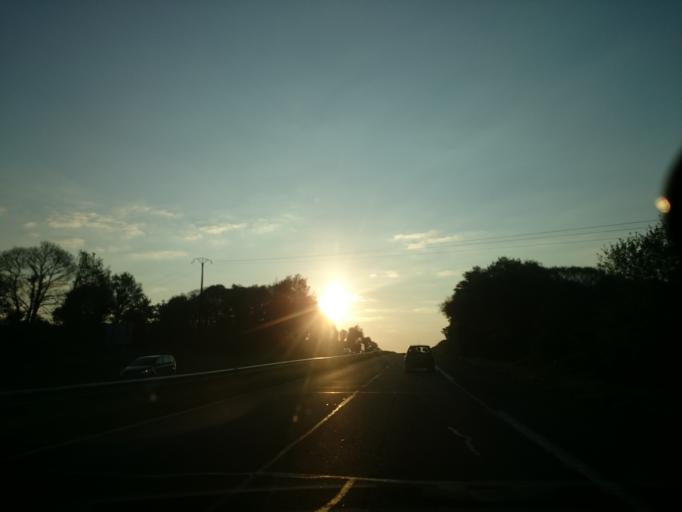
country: FR
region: Brittany
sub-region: Departement du Finistere
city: Loperhet
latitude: 48.3828
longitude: -4.3338
